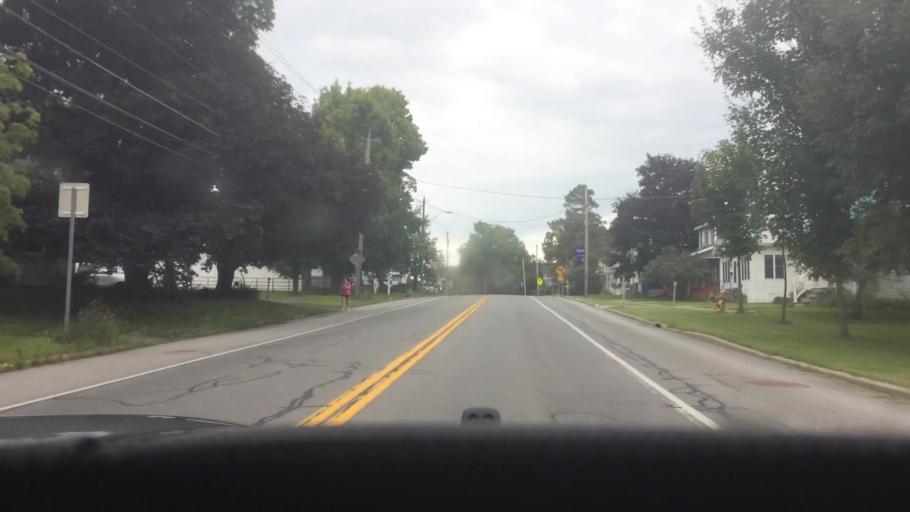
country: US
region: New York
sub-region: St. Lawrence County
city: Ogdensburg
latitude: 44.6221
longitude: -75.4117
